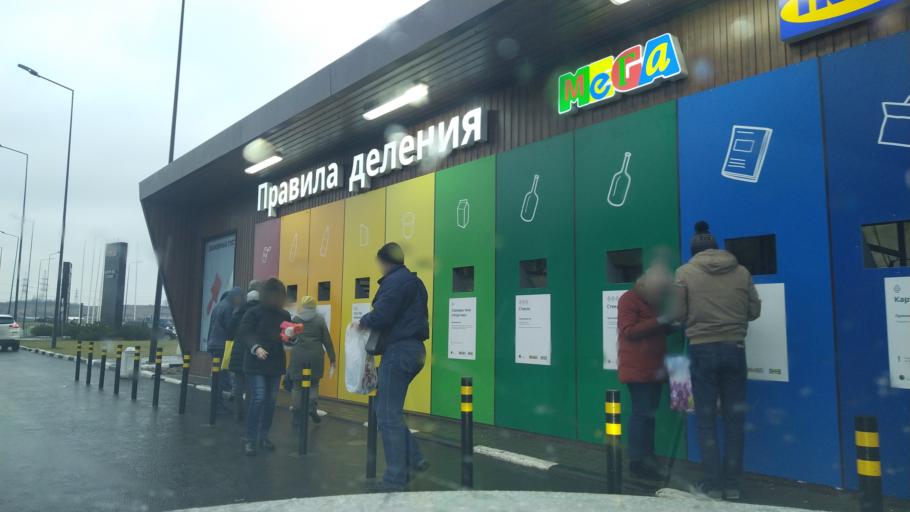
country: RU
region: Leningrad
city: Bugry
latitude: 60.0933
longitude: 30.3807
